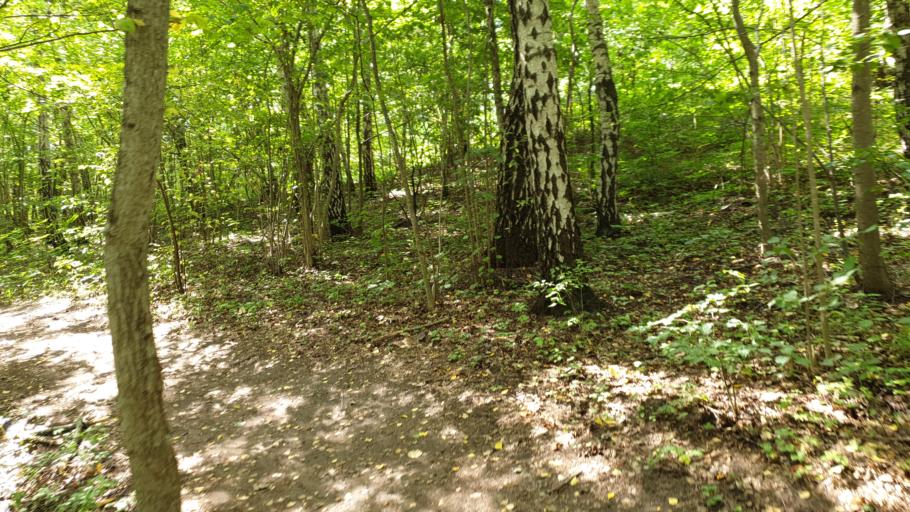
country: LT
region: Vilnius County
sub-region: Vilniaus Rajonas
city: Vievis
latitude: 54.8253
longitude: 24.9400
